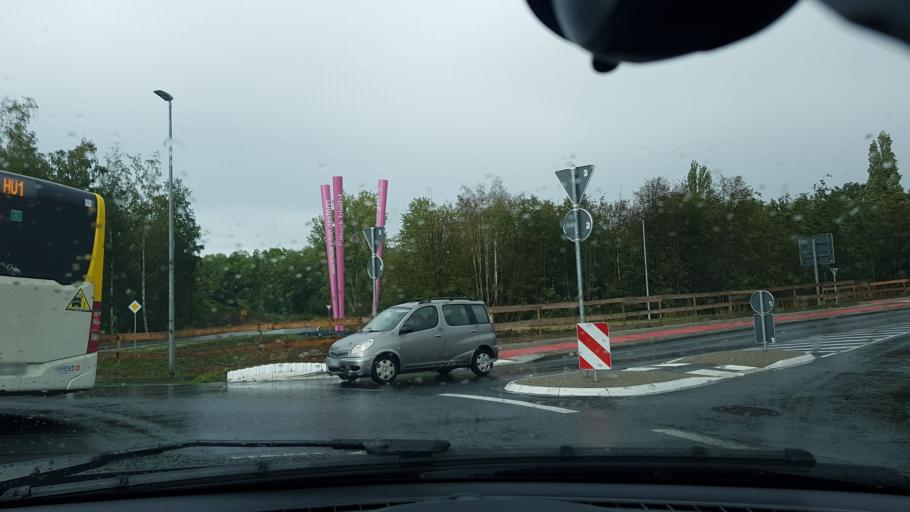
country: DE
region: North Rhine-Westphalia
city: Huckelhoven
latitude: 51.0535
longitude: 6.2154
